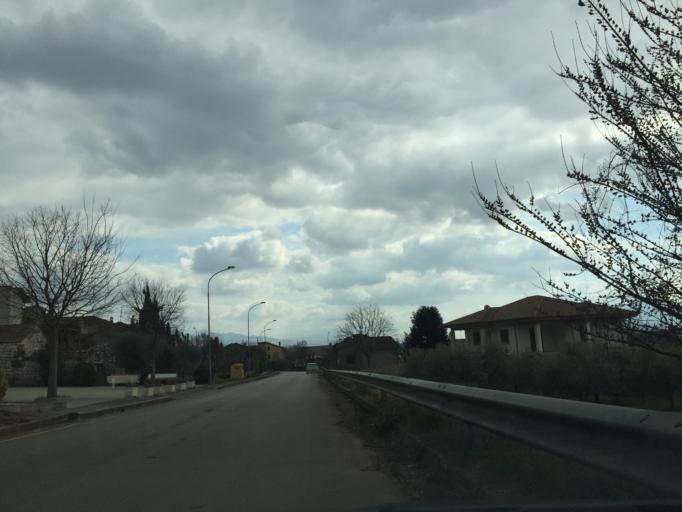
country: IT
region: Latium
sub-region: Provincia di Frosinone
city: Villa Santa Lucia
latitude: 41.4912
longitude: 13.7830
